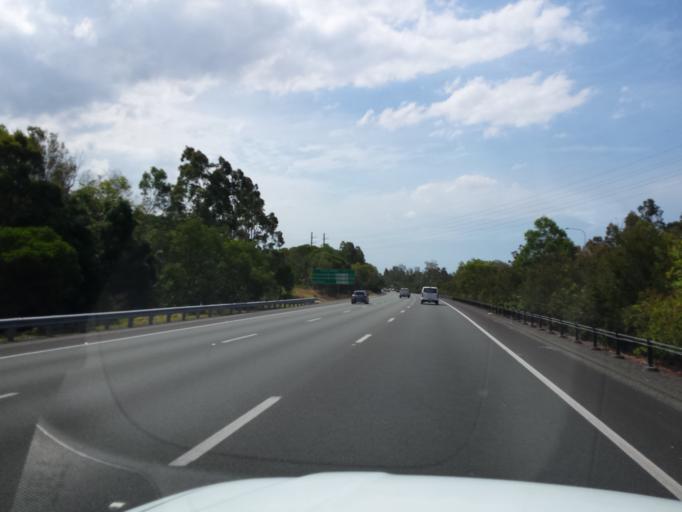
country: AU
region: Queensland
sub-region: Gold Coast
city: Nerang
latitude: -27.9589
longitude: 153.3449
